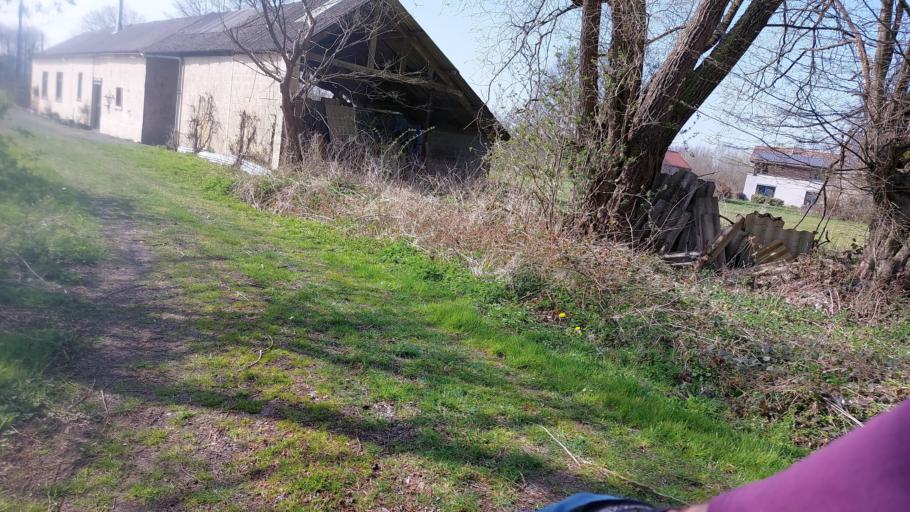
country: BE
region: Wallonia
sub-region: Province du Hainaut
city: Soignies
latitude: 50.5367
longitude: 4.0289
